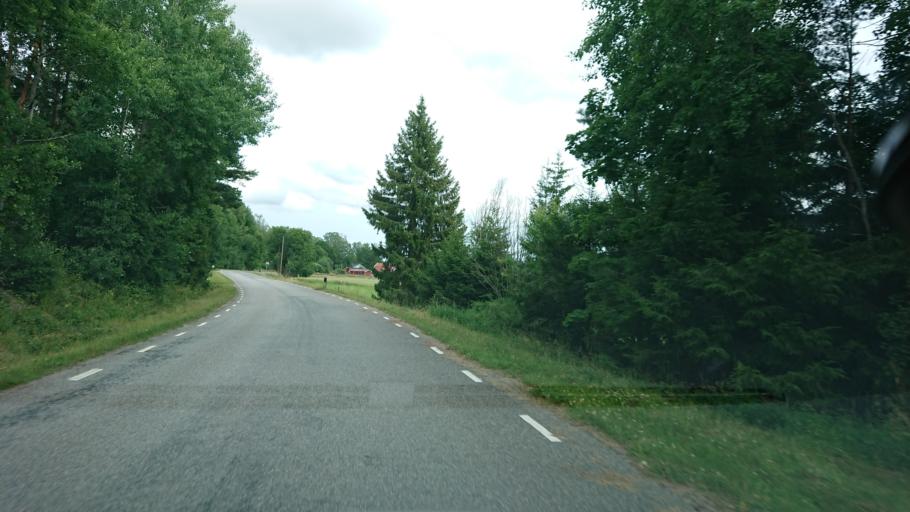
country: SE
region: Uppsala
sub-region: Osthammars Kommun
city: Bjorklinge
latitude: 60.0034
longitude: 17.4587
